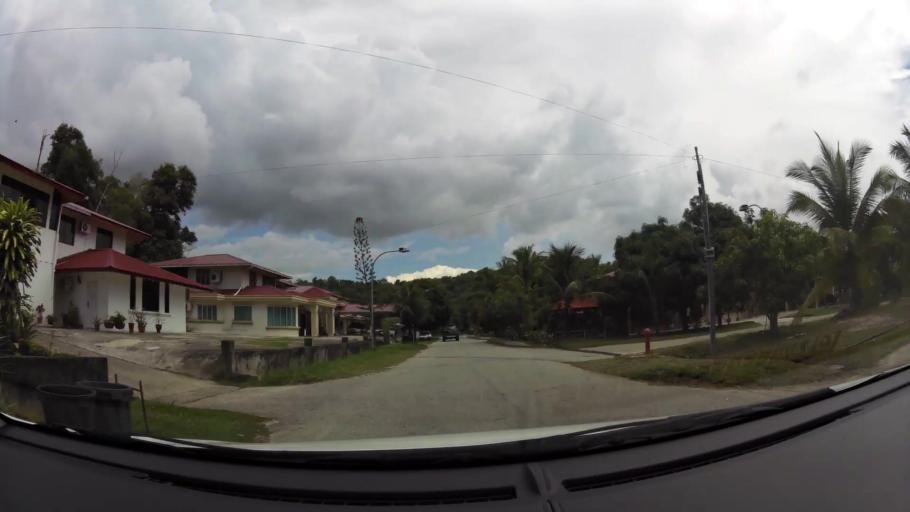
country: BN
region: Brunei and Muara
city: Bandar Seri Begawan
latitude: 4.9849
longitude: 114.9316
